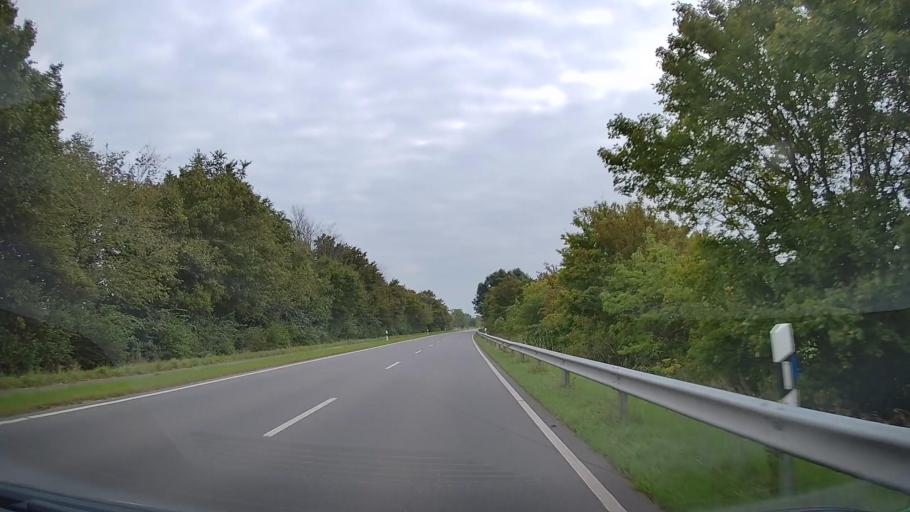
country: DE
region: Schleswig-Holstein
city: Krummbek
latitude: 54.4001
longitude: 10.4070
